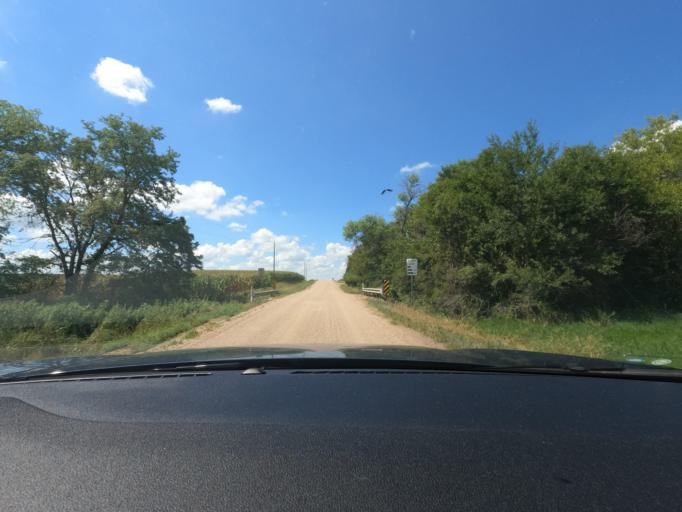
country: US
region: Nebraska
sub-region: Saunders County
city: Wahoo
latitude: 41.2492
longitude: -96.5492
